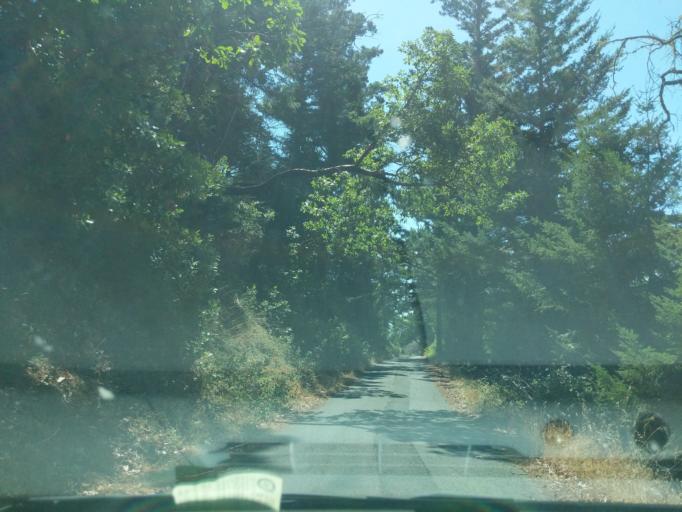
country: US
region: California
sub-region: Sonoma County
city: Monte Rio
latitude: 38.5316
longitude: -123.2244
